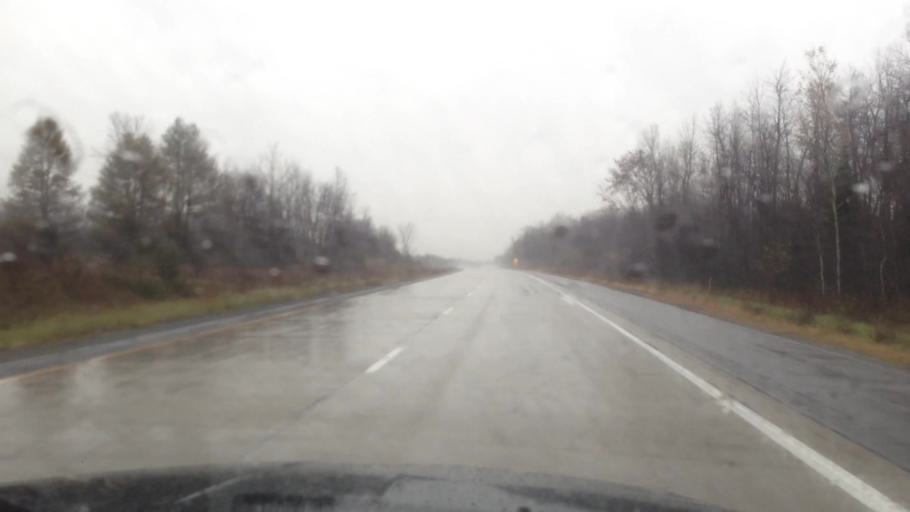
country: CA
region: Ontario
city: Hawkesbury
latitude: 45.4973
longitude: -74.6047
